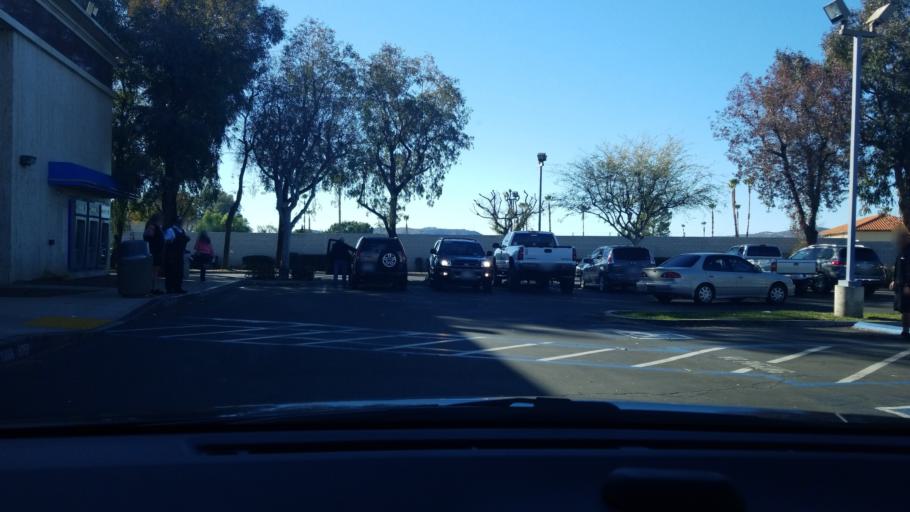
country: US
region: California
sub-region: Riverside County
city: Hemet
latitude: 33.7457
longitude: -117.0158
